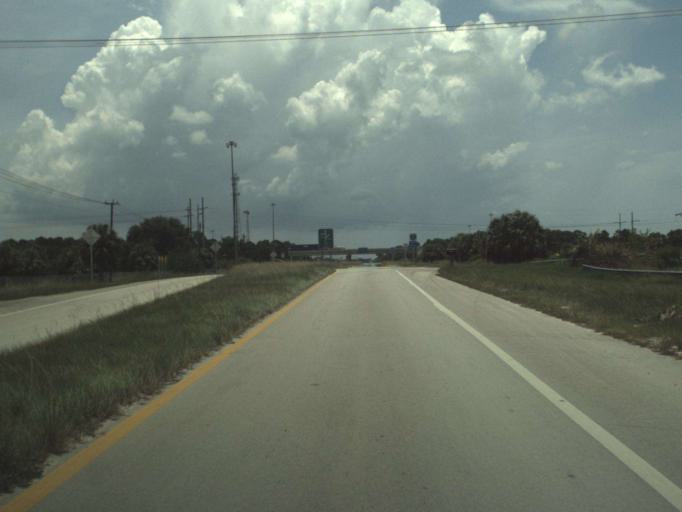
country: US
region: Florida
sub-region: Saint Lucie County
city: Lakewood Park
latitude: 27.5217
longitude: -80.4565
